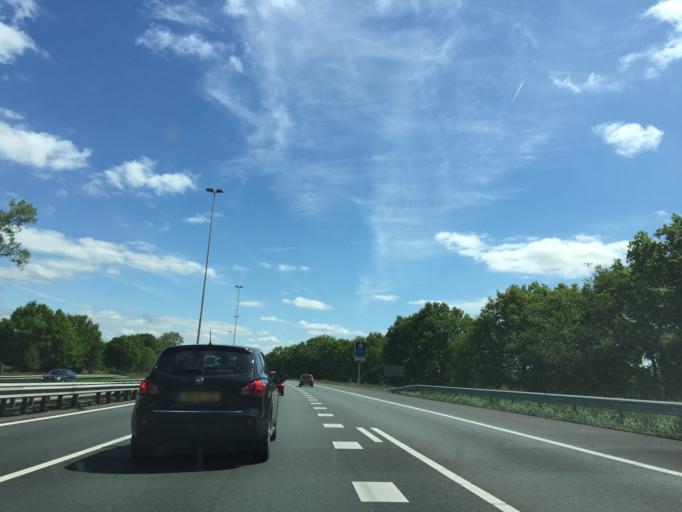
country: NL
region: Utrecht
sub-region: Gemeente Leusden
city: Leusden
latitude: 52.1679
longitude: 5.4455
